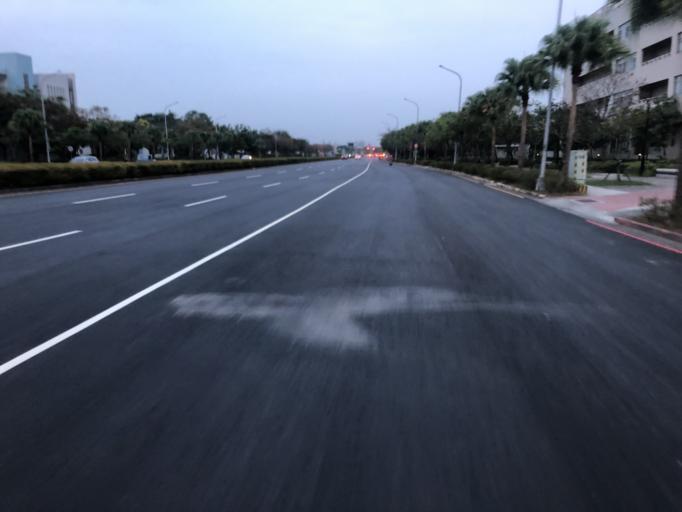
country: TW
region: Taiwan
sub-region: Tainan
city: Tainan
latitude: 23.1045
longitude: 120.2907
